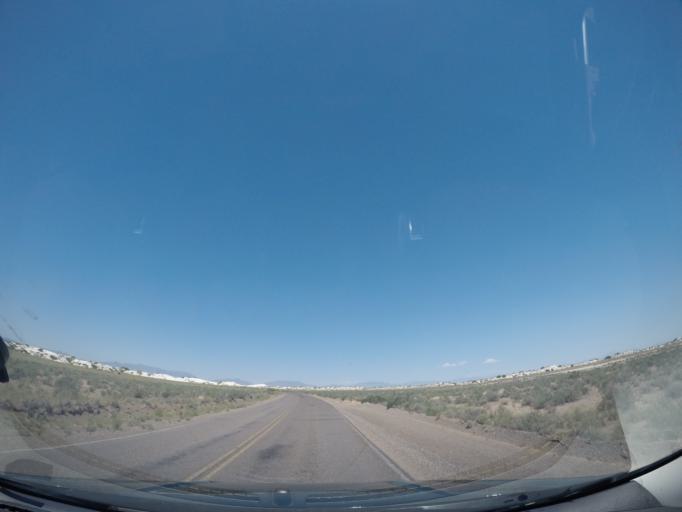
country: US
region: New Mexico
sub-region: Otero County
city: Holloman Air Force Base
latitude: 32.7955
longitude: -106.2084
